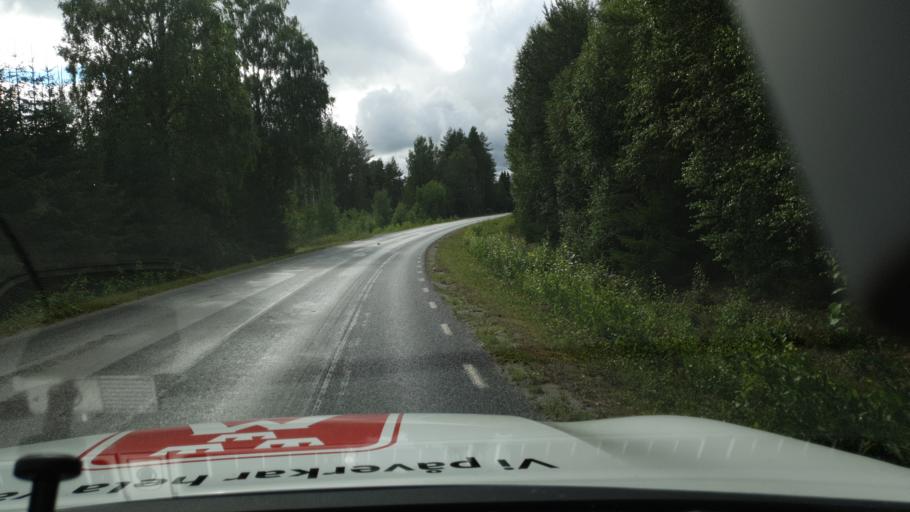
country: SE
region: Vaesterbotten
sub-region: Skelleftea Kommun
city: Soedra Bergsbyn
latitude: 64.5813
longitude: 21.0132
